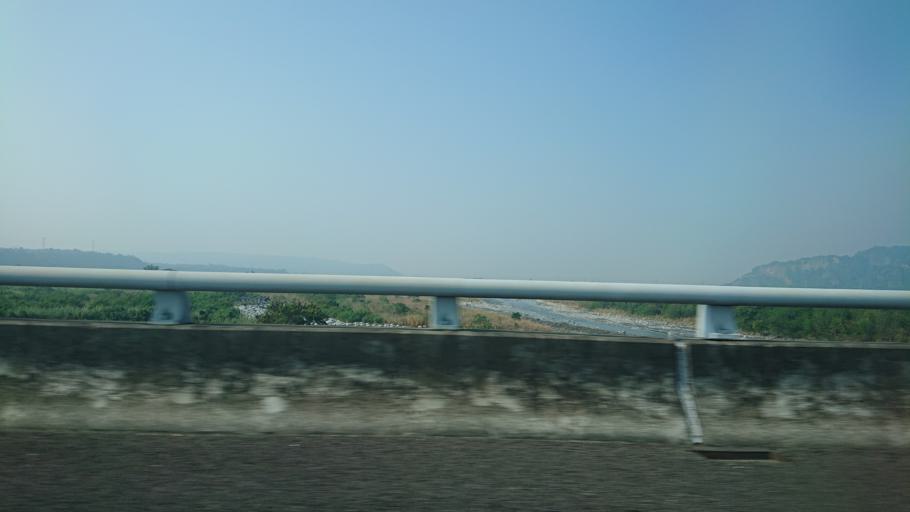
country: TW
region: Taiwan
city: Lugu
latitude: 23.8008
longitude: 120.6995
